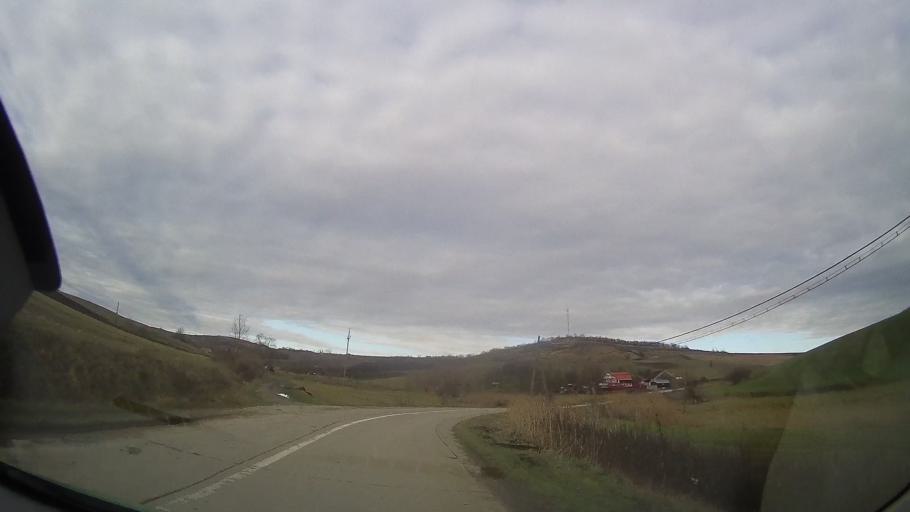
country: RO
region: Bistrita-Nasaud
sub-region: Comuna Micestii de Campie
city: Micestii de Campie
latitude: 46.8437
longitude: 24.3003
